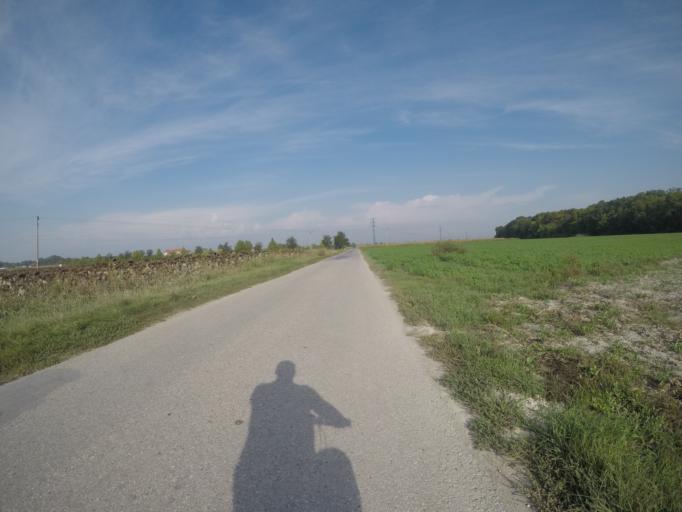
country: SK
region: Trnavsky
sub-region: Okres Dunajska Streda
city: Velky Meder
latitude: 47.8460
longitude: 17.7507
